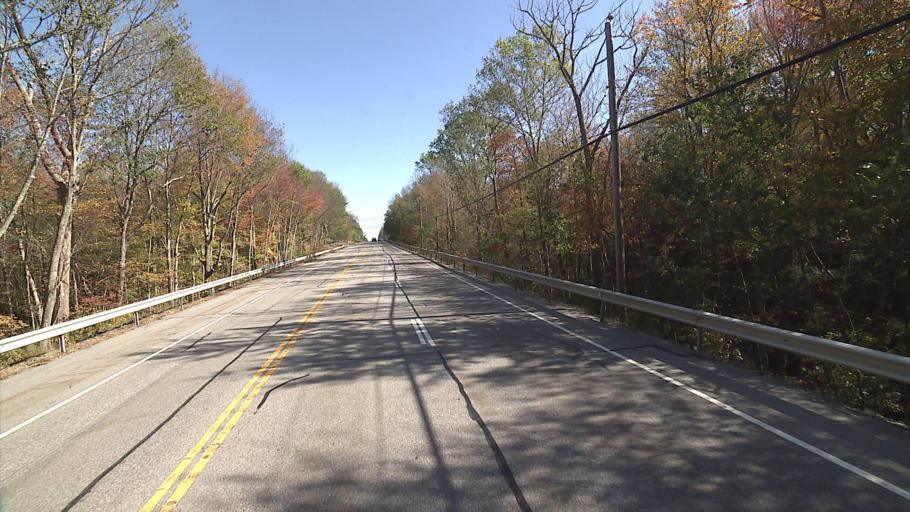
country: US
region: Connecticut
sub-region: Windham County
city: Wauregan
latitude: 41.7797
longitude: -72.0275
